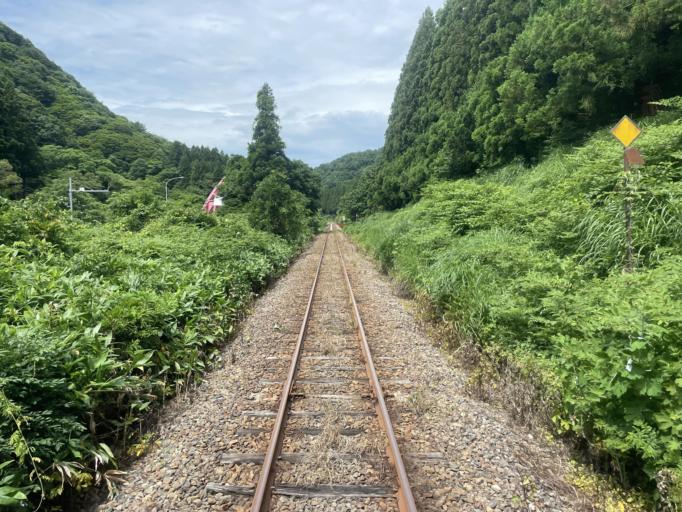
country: JP
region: Niigata
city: Murakami
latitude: 38.0800
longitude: 139.6542
